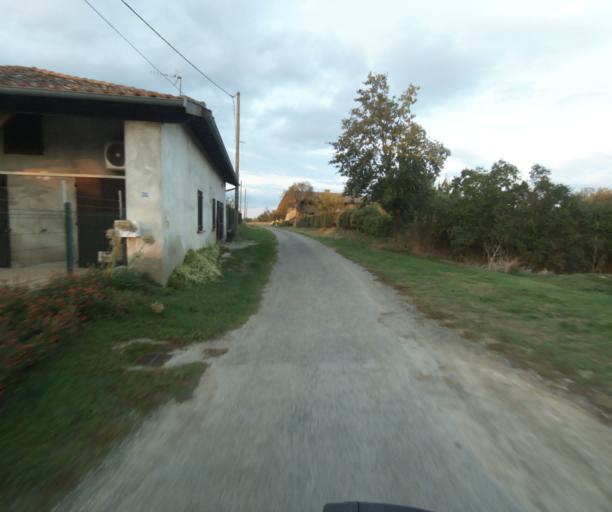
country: FR
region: Midi-Pyrenees
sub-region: Departement du Tarn-et-Garonne
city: Verdun-sur-Garonne
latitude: 43.8355
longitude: 1.2453
